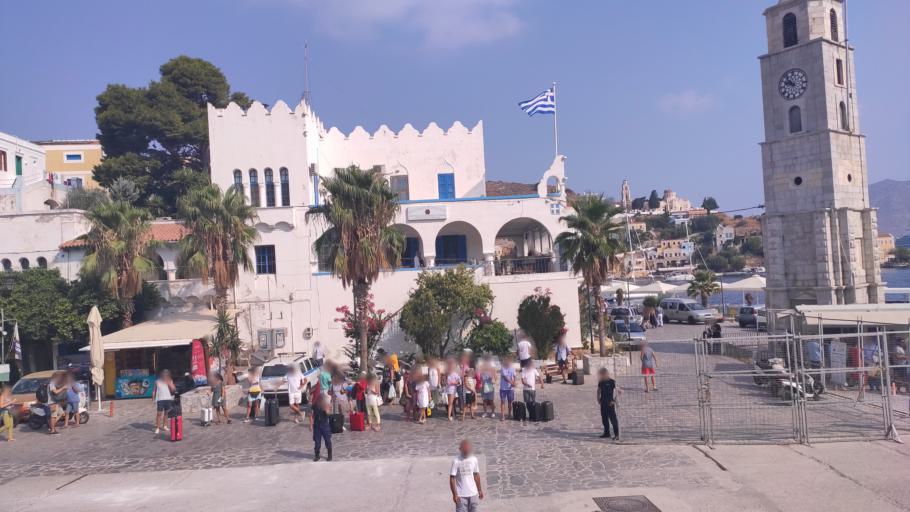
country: GR
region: South Aegean
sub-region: Nomos Dodekanisou
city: Symi
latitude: 36.6176
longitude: 27.8390
